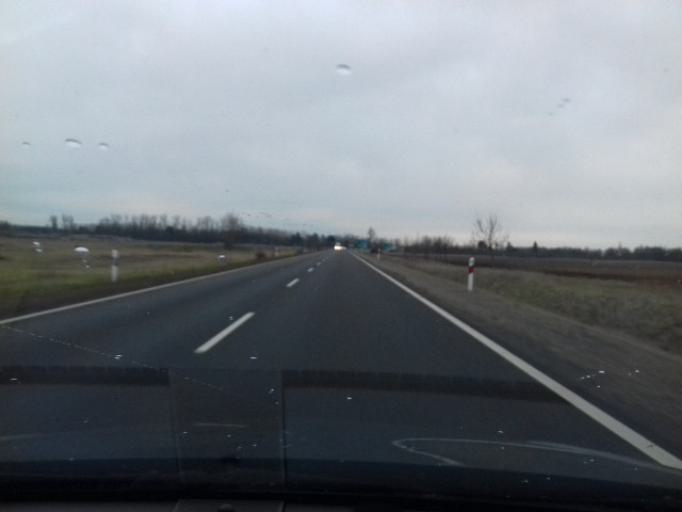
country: HU
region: Szabolcs-Szatmar-Bereg
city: Nyirpazony
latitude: 47.9572
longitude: 21.8180
